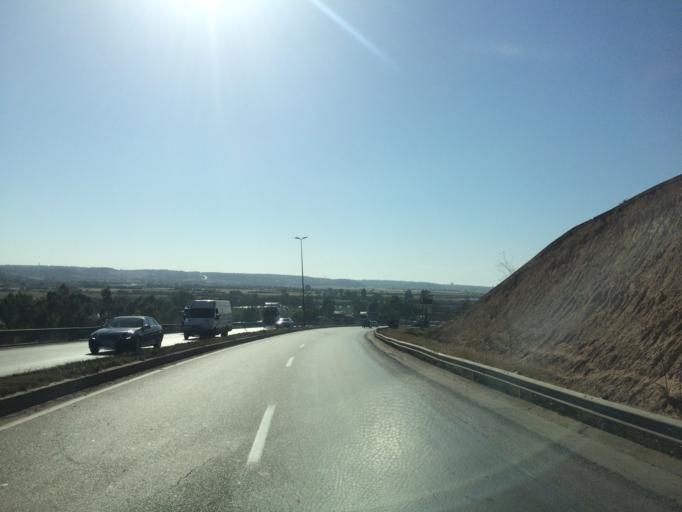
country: MA
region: Rabat-Sale-Zemmour-Zaer
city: Sale
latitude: 33.9844
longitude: -6.7583
